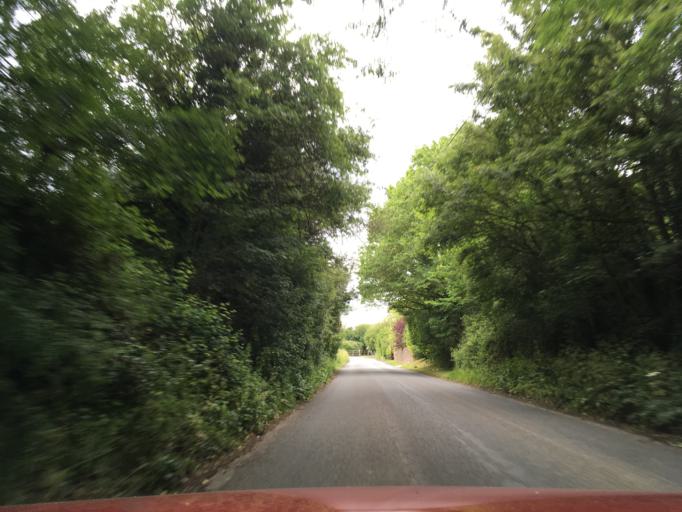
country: GB
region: England
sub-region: Wiltshire
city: Minety
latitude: 51.6447
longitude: -1.9931
